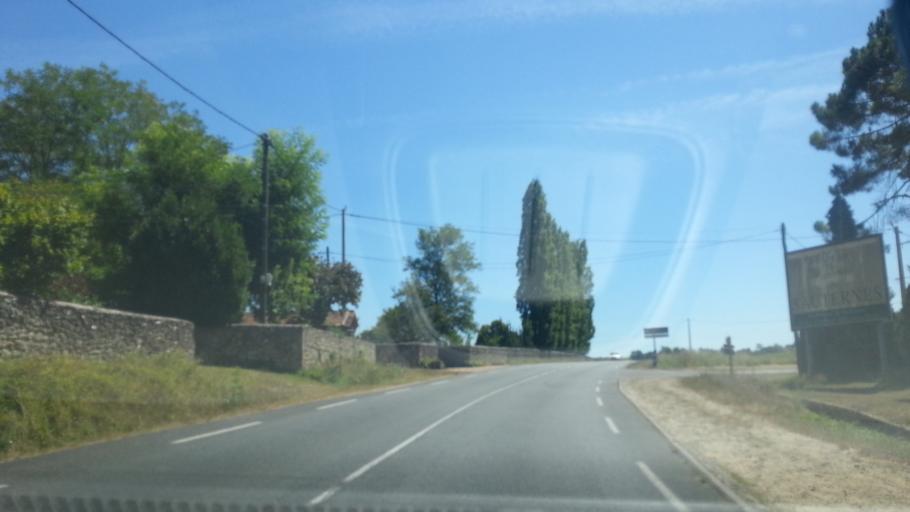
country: FR
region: Aquitaine
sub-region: Departement de la Gironde
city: Illats
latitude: 44.5580
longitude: -0.3542
